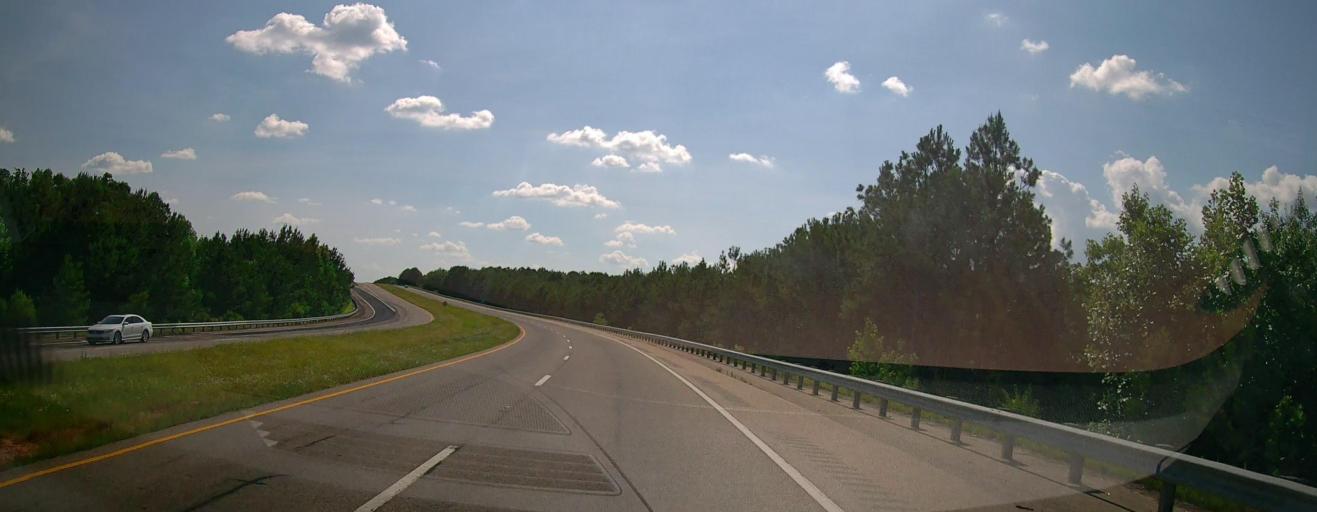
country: US
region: Georgia
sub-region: Henry County
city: Hampton
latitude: 33.3794
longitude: -84.2867
